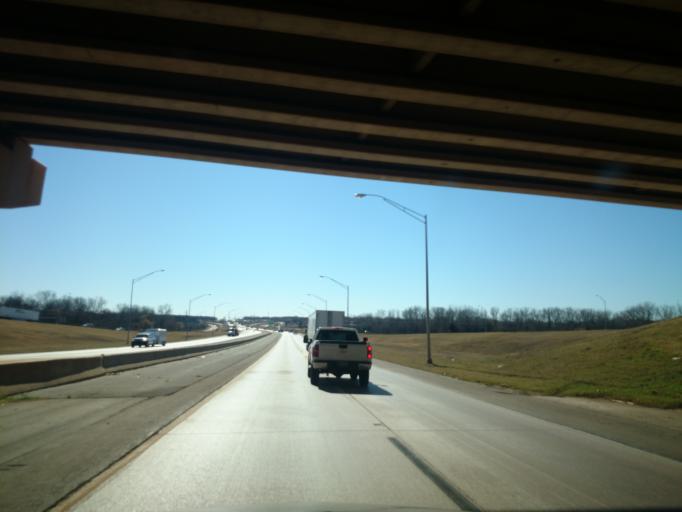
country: US
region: Oklahoma
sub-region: Oklahoma County
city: Edmond
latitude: 35.6522
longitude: -97.4244
